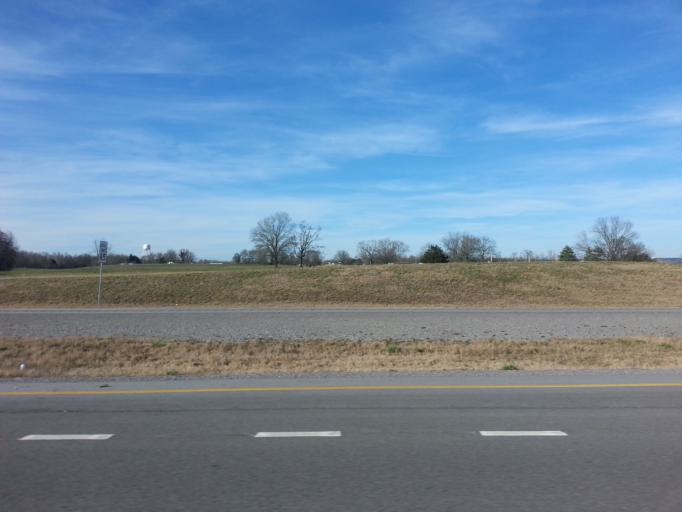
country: US
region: Tennessee
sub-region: Warren County
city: McMinnville
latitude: 35.7148
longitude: -85.8558
